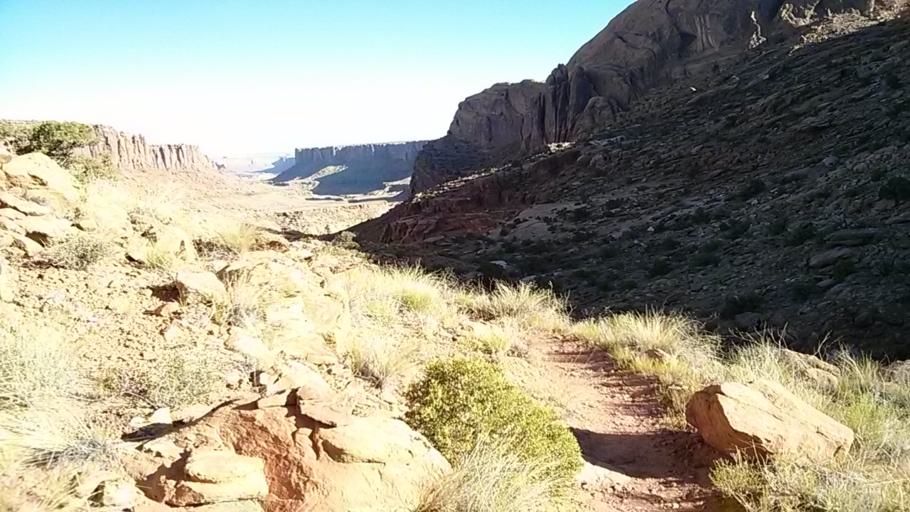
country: US
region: Utah
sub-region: Grand County
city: Moab
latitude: 38.4294
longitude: -109.9458
